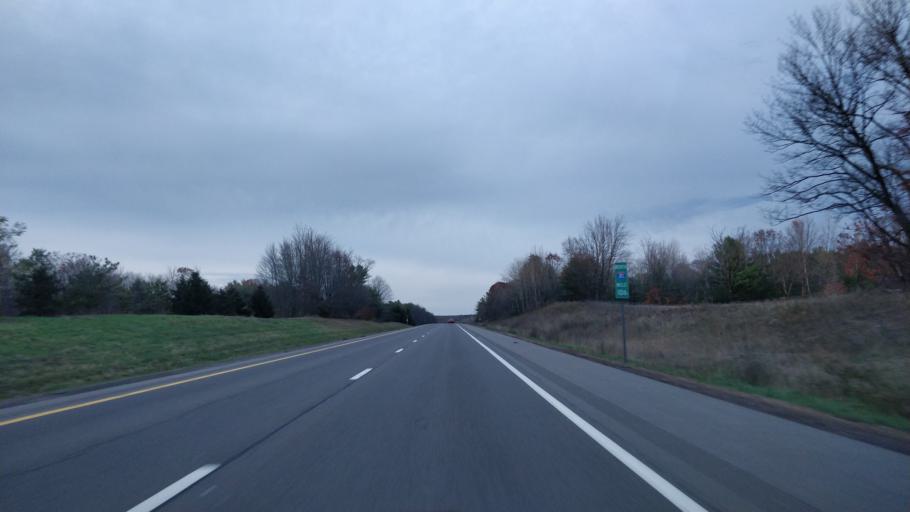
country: US
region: New York
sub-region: Oswego County
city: Central Square
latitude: 43.3190
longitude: -76.1278
